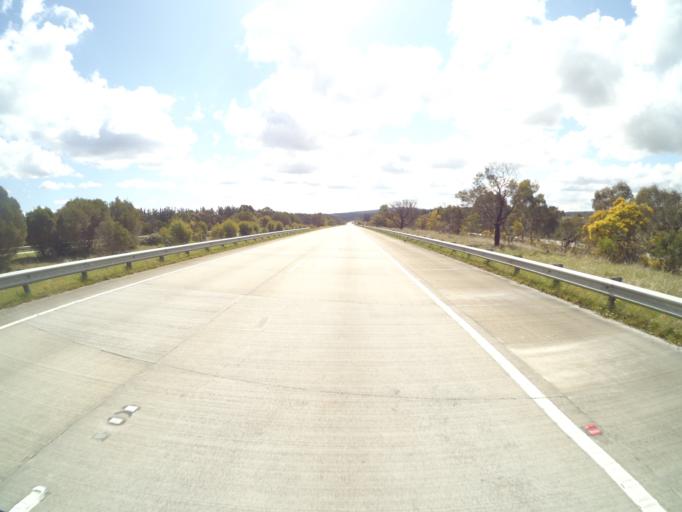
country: AU
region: New South Wales
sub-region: Wingecarribee
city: Moss Vale
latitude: -34.4966
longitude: 150.3110
